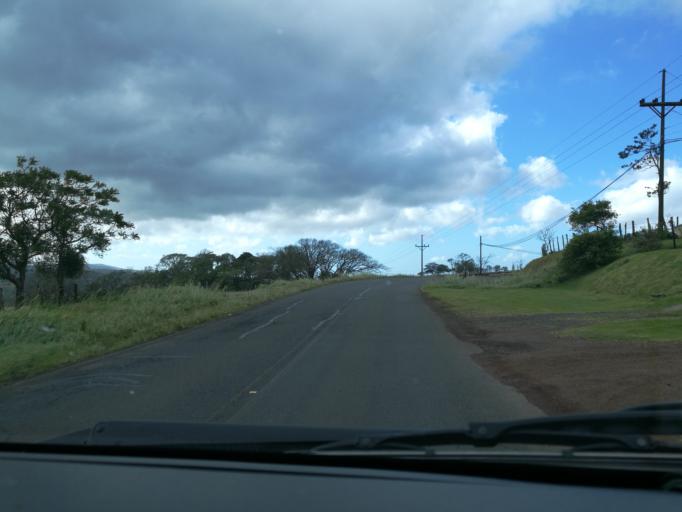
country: CR
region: Alajuela
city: Bijagua
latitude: 10.6782
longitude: -85.0898
